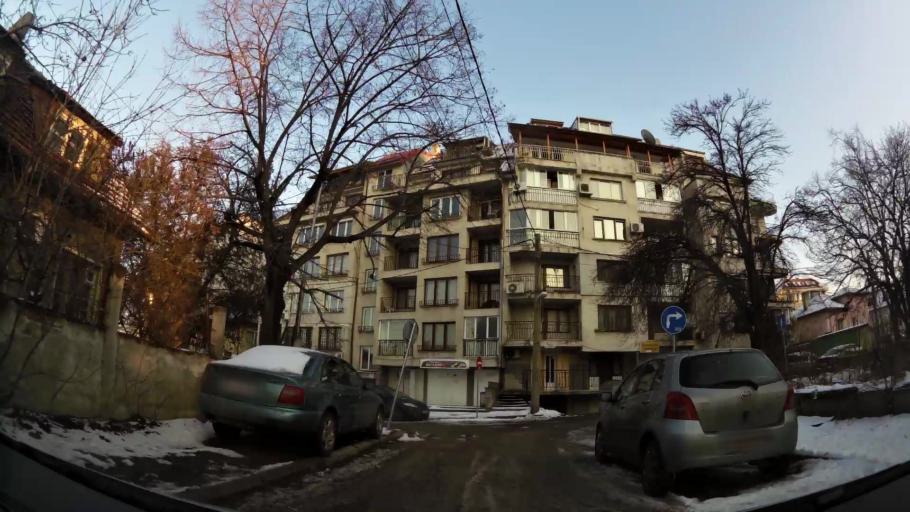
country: BG
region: Sofia-Capital
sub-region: Stolichna Obshtina
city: Sofia
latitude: 42.6940
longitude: 23.3635
